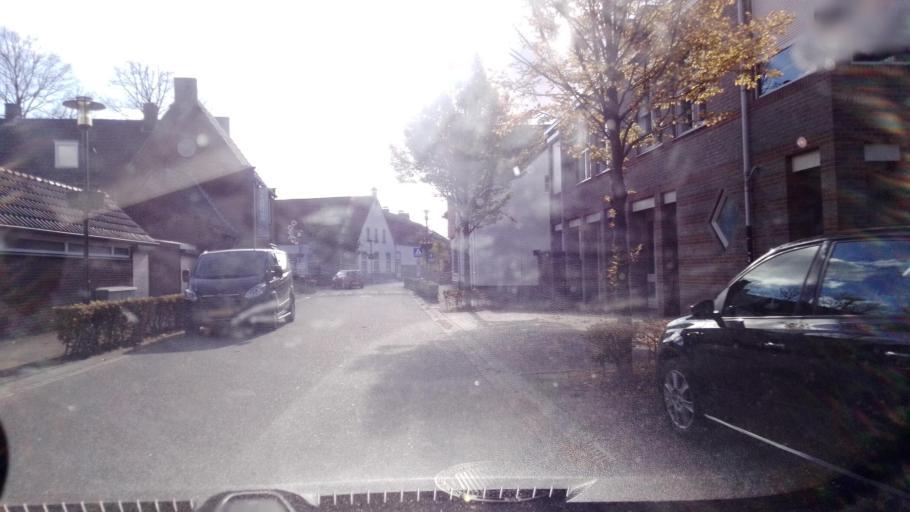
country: NL
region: Limburg
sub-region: Gemeente Venlo
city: Venlo
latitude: 51.4201
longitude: 6.1473
